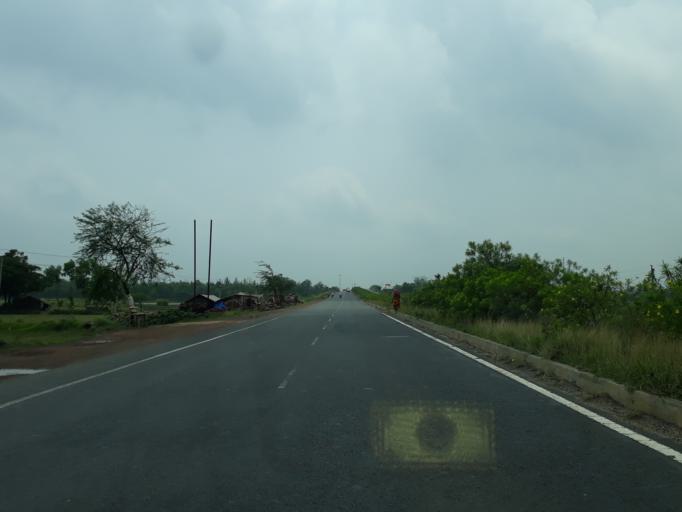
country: IN
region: West Bengal
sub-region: Purba Medinipur
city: Mahishadal
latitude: 22.1459
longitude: 87.9691
